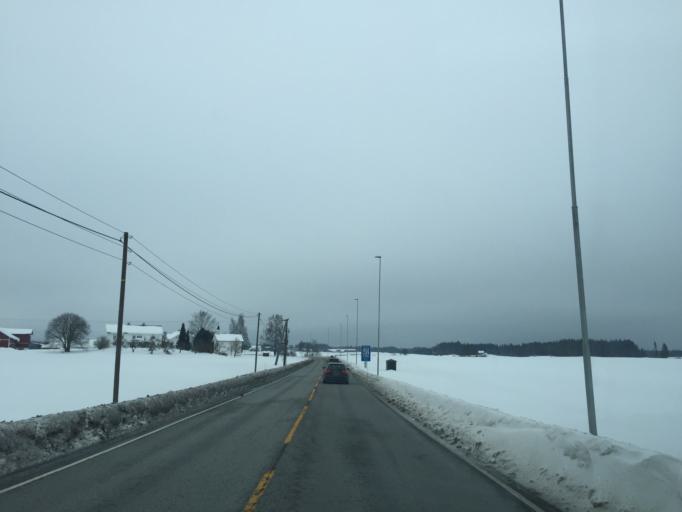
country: NO
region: Hedmark
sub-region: Loten
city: Loten
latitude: 60.8386
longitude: 11.3634
